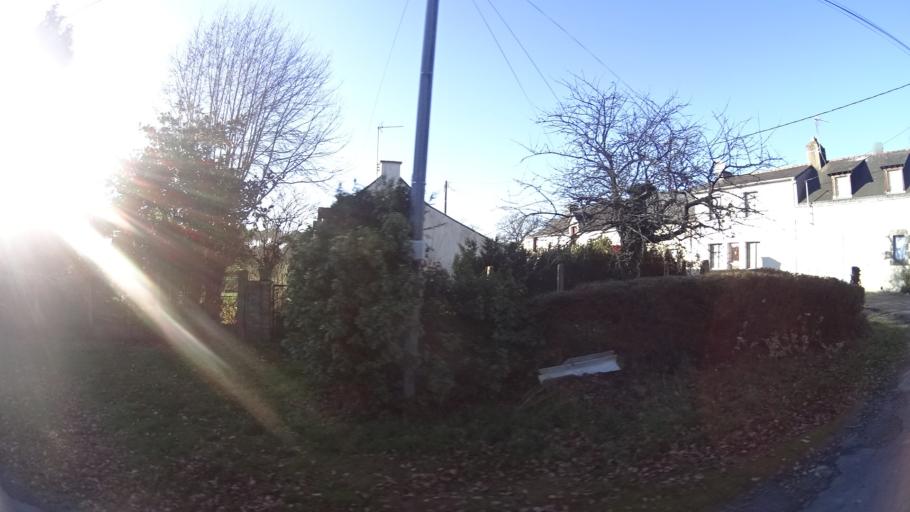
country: FR
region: Brittany
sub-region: Departement du Morbihan
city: Allaire
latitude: 47.6619
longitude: -2.1836
